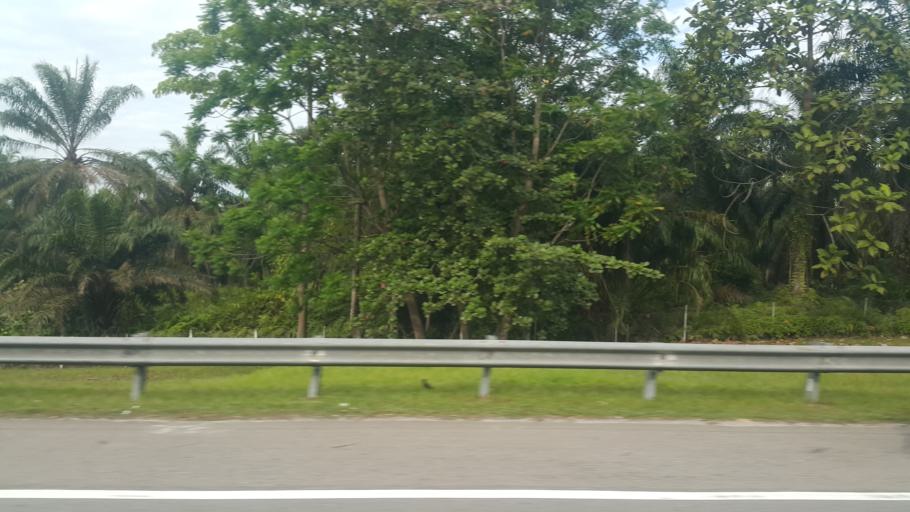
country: MY
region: Johor
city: Pekan Nenas
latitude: 1.3860
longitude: 103.5925
